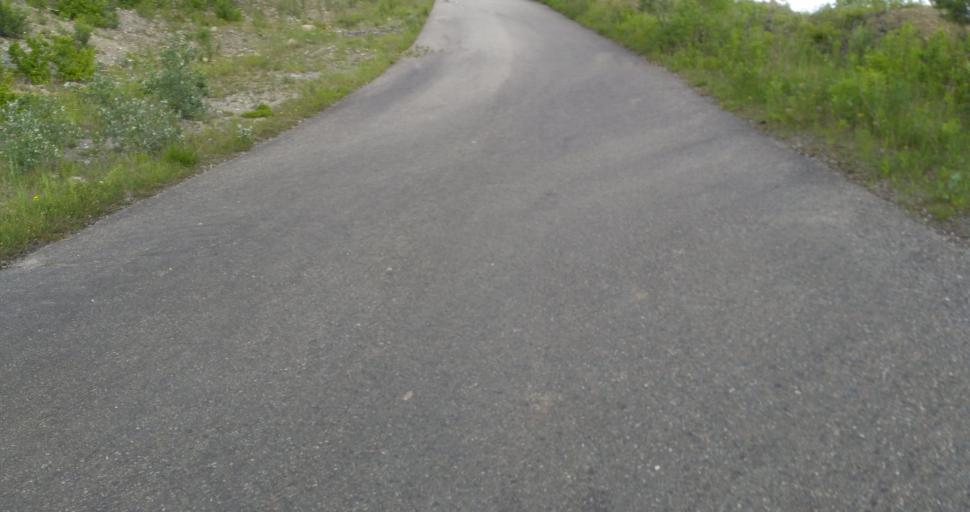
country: CZ
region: South Moravian
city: Bilovice nad Svitavou
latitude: 49.2203
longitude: 16.6695
